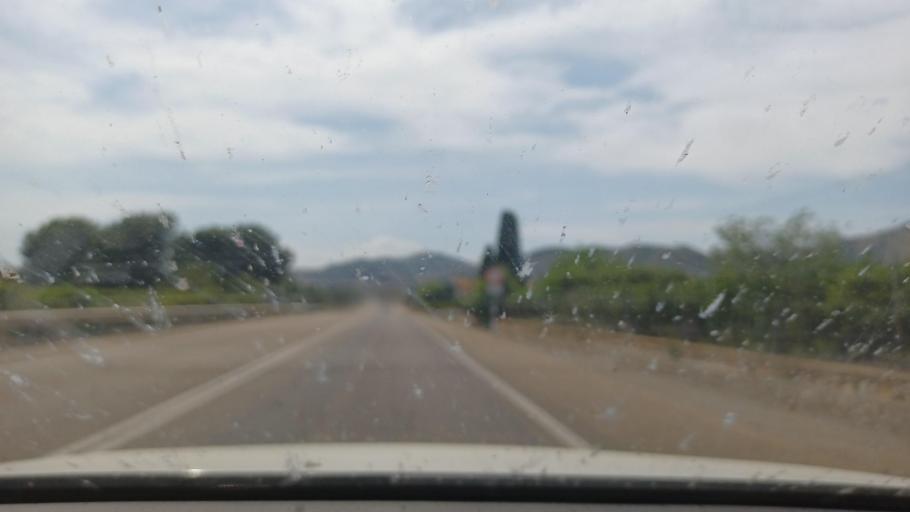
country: ES
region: Valencia
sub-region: Provincia de Castello
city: Castello de la Plana
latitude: 40.0254
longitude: -0.0125
